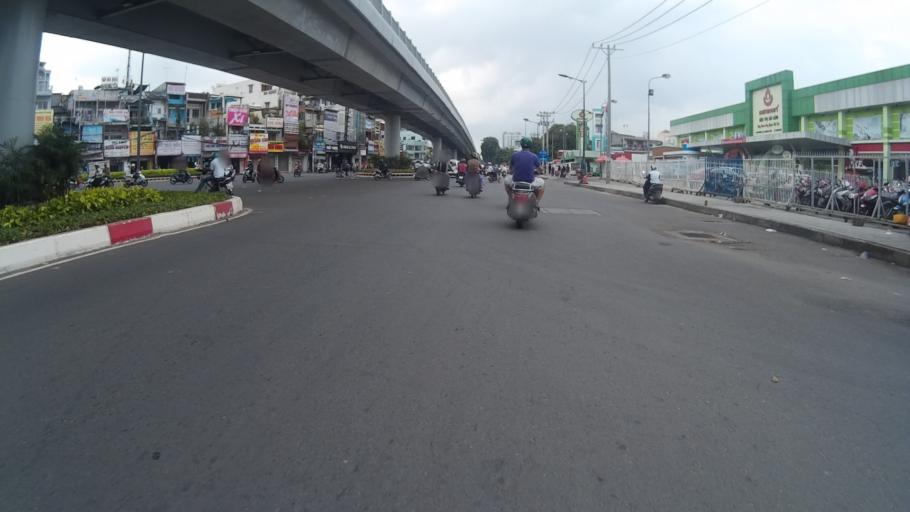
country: VN
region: Ho Chi Minh City
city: Quan Muoi
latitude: 10.7684
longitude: 106.6683
